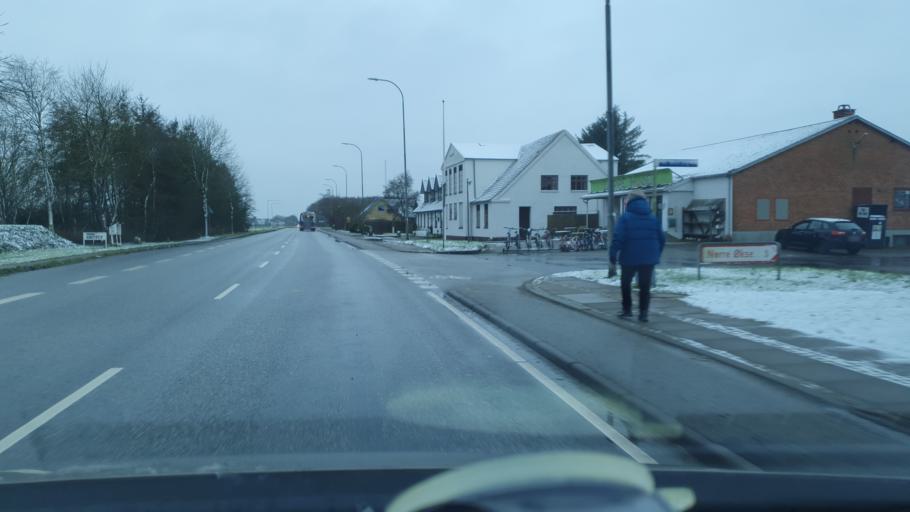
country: DK
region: North Denmark
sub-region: Jammerbugt Kommune
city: Kas
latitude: 57.1216
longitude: 9.6214
